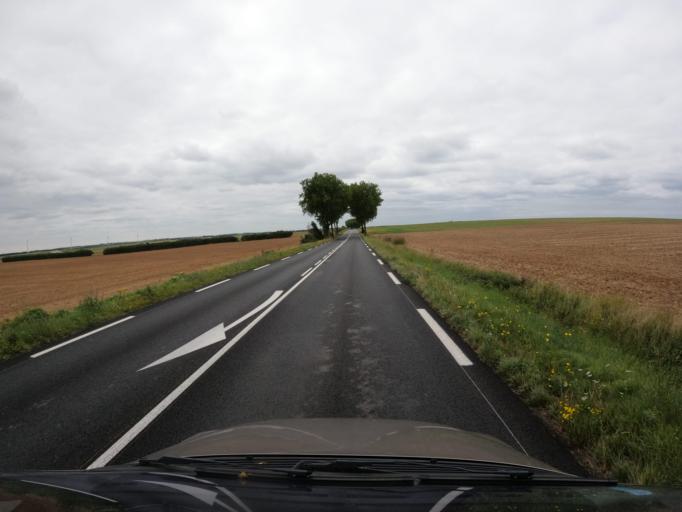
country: FR
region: Pays de la Loire
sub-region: Departement de la Vendee
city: Saint-Martin-sous-Mouzeuil
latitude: 46.5174
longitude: -0.9753
